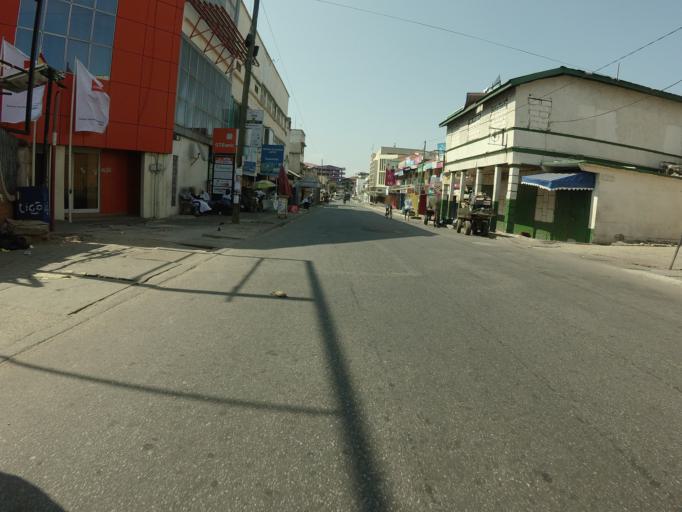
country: GH
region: Greater Accra
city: Accra
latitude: 5.5436
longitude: -0.2070
